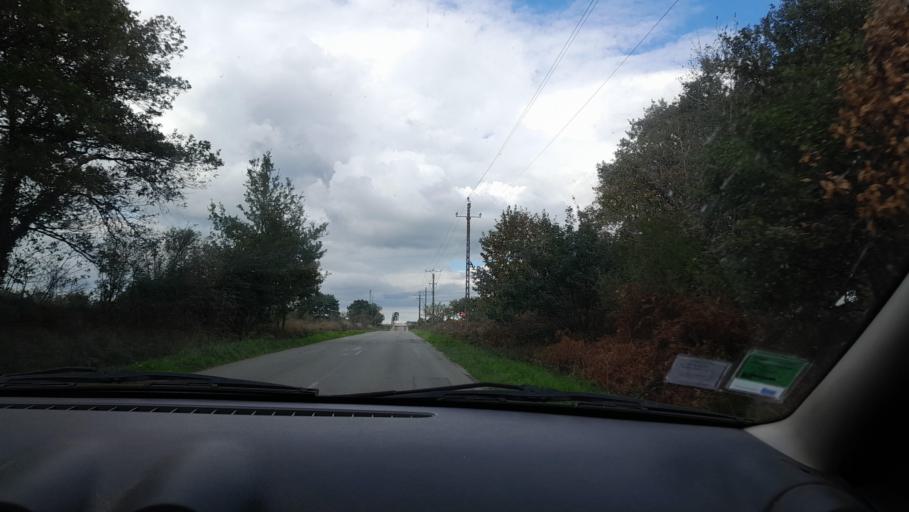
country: FR
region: Brittany
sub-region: Departement d'Ille-et-Vilaine
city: Le Pertre
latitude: 48.0086
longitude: -1.0386
